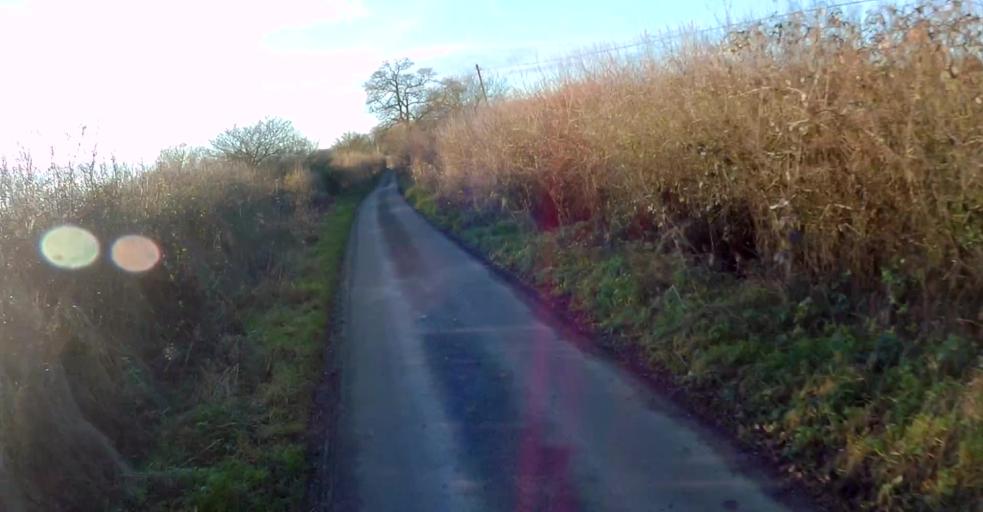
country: GB
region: England
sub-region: Hampshire
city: Hook
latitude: 51.3080
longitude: -0.9976
